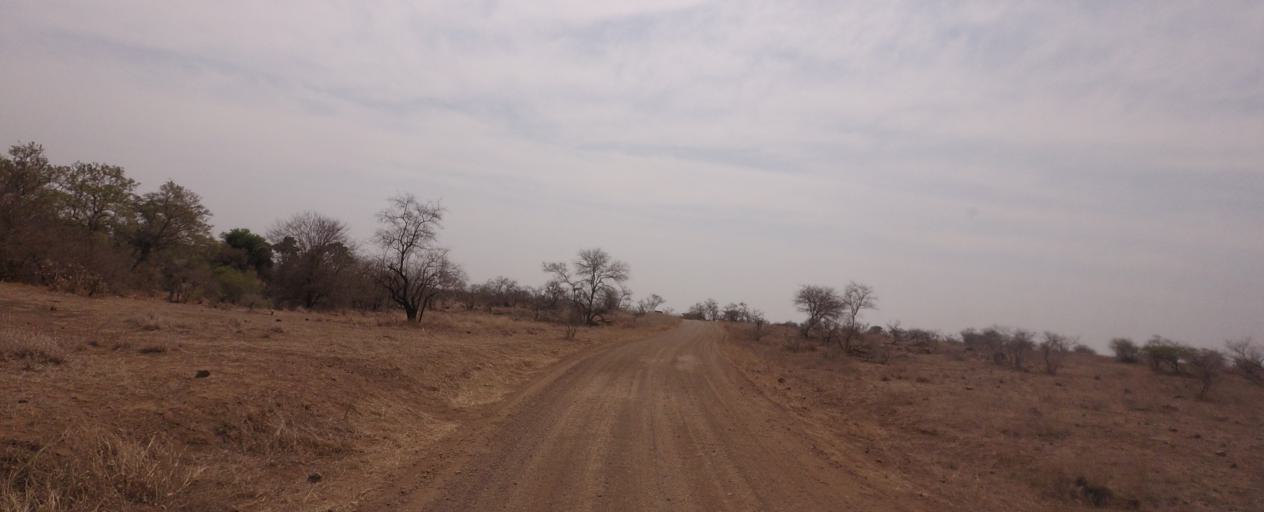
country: ZA
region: Limpopo
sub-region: Mopani District Municipality
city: Phalaborwa
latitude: -24.2597
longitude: 31.6513
